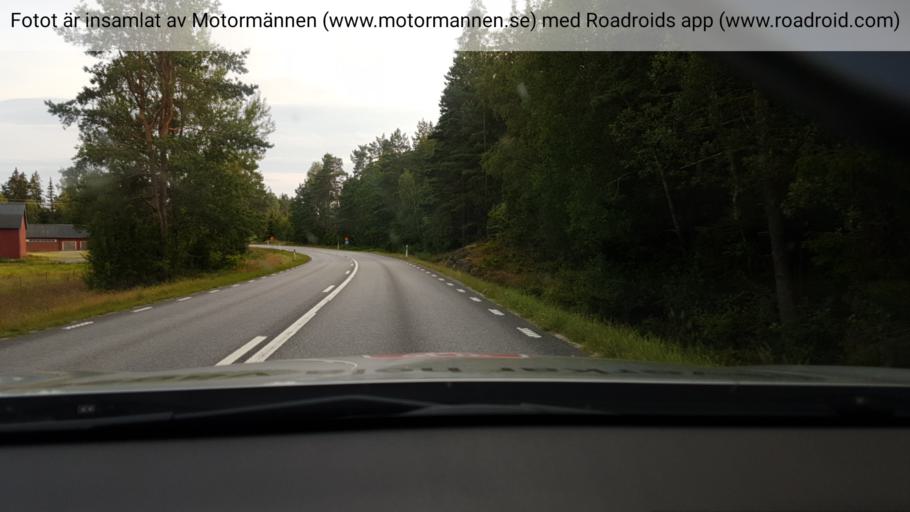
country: SE
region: Vaestra Goetaland
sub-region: Uddevalla Kommun
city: Uddevalla
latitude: 58.3888
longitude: 11.9944
